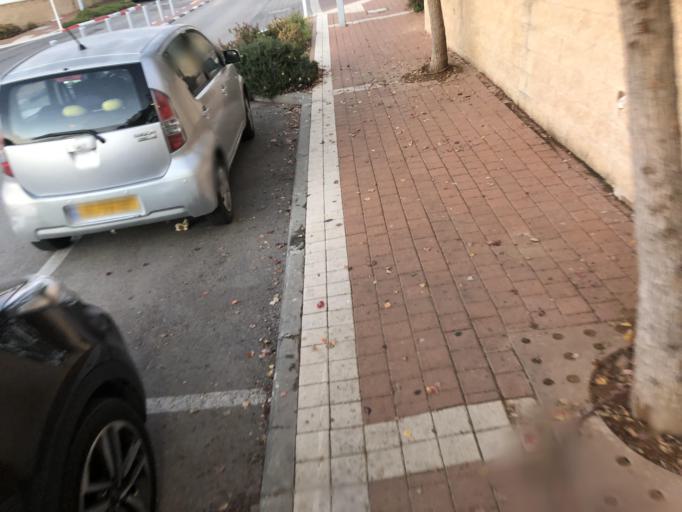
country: IL
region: Northern District
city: `Akko
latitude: 32.9347
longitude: 35.0900
